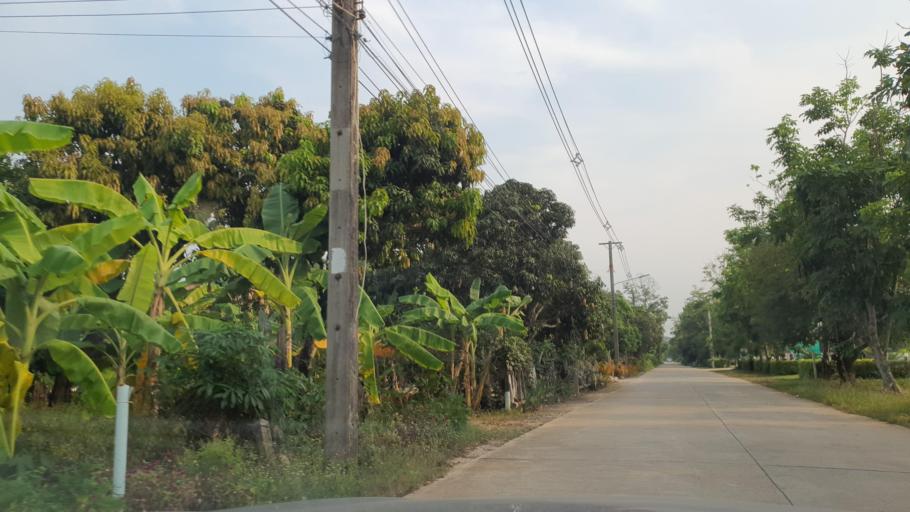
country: TH
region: Rayong
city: Rayong
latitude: 12.6095
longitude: 101.4007
